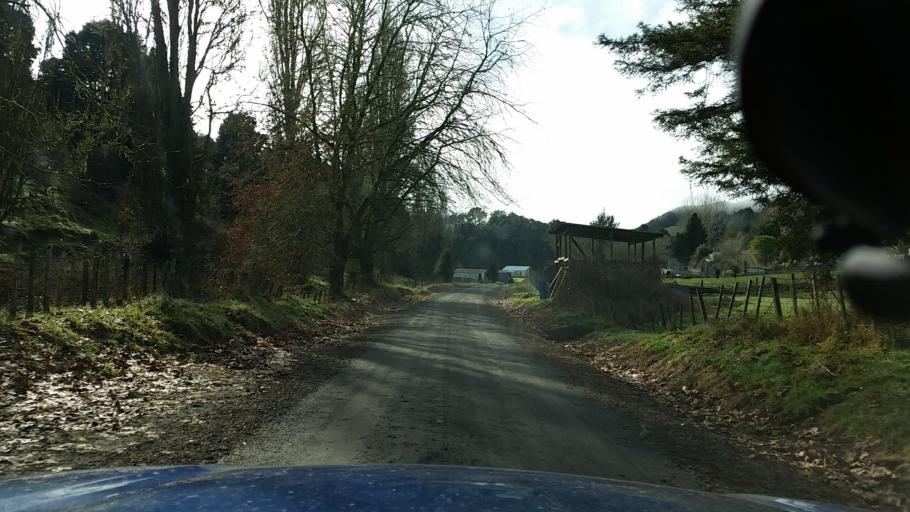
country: NZ
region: Taranaki
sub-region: New Plymouth District
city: Waitara
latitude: -39.0336
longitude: 174.7986
